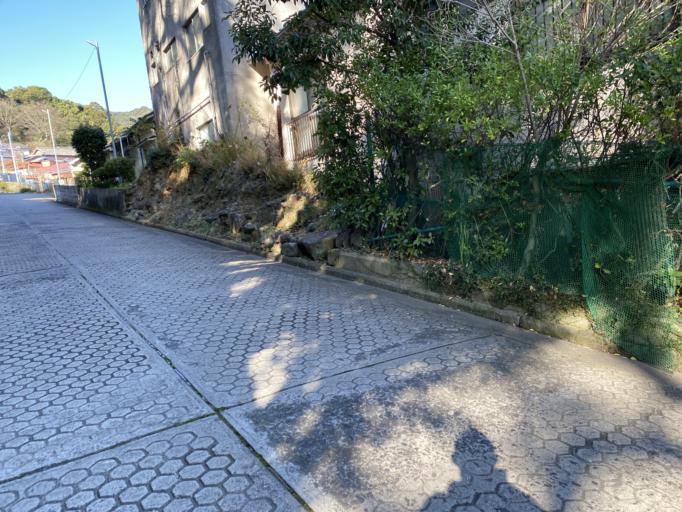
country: JP
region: Nagasaki
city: Nagasaki-shi
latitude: 32.7586
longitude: 129.8605
